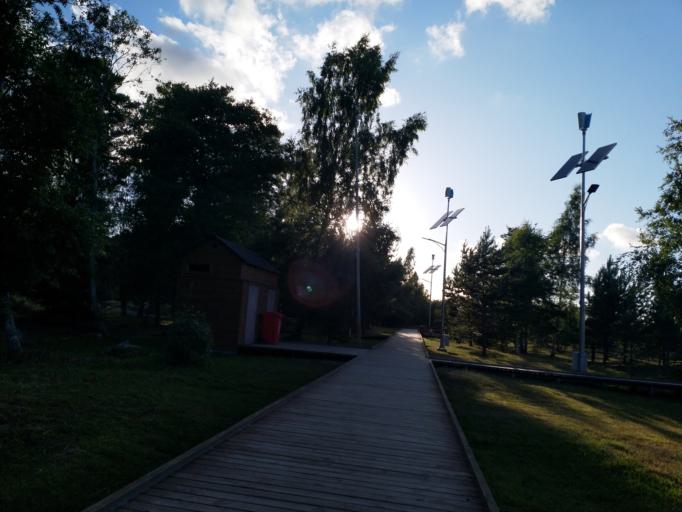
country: LV
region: Rojas
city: Roja
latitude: 57.5104
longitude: 22.8002
